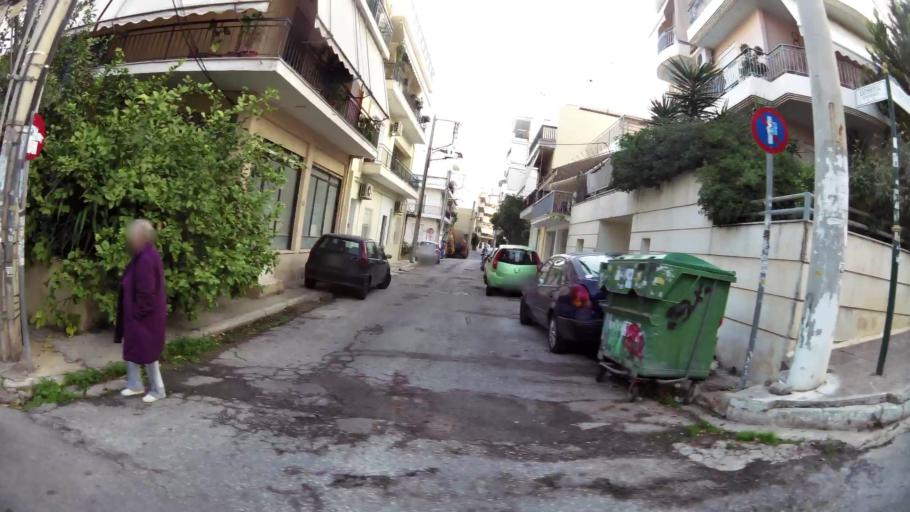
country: GR
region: Attica
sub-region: Nomarchia Athinas
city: Ymittos
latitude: 37.9427
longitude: 23.7460
